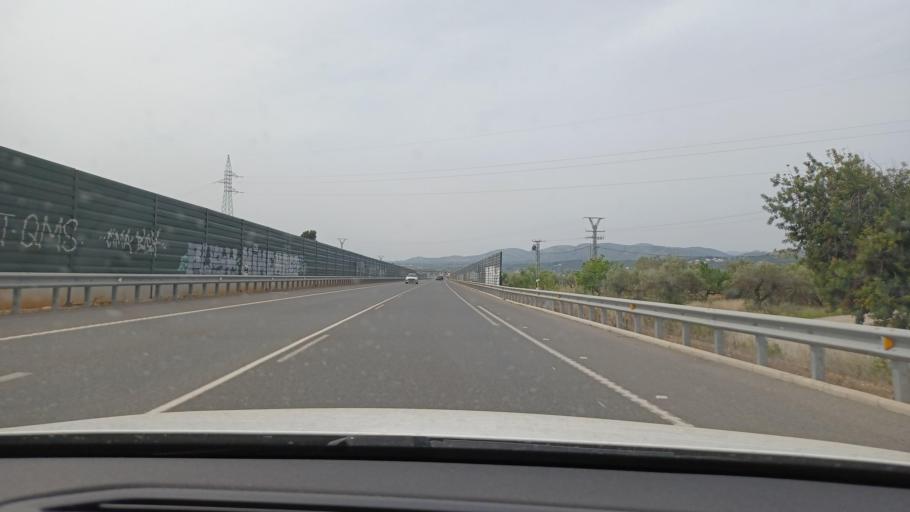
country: ES
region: Valencia
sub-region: Provincia de Castello
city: Benicarlo
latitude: 40.4287
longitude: 0.4010
